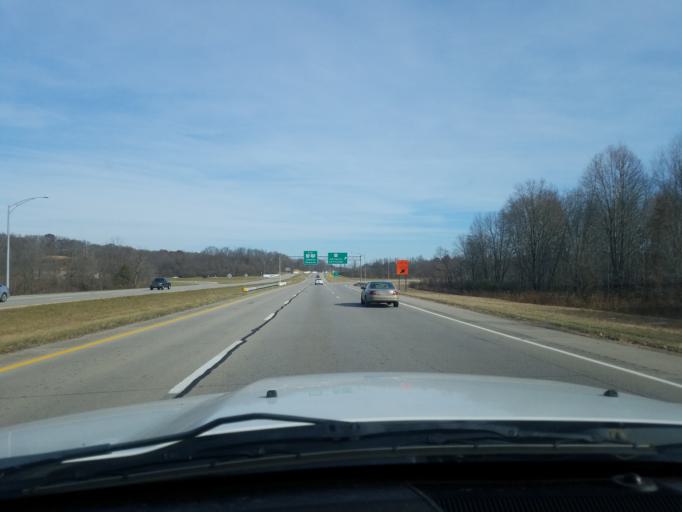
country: US
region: Ohio
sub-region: Jackson County
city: Jackson
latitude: 39.0427
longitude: -82.6183
